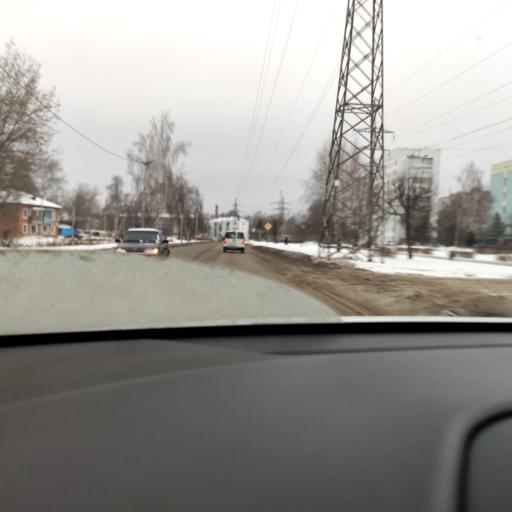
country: RU
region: Tatarstan
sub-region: Zelenodol'skiy Rayon
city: Zelenodolsk
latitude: 55.8520
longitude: 48.4874
